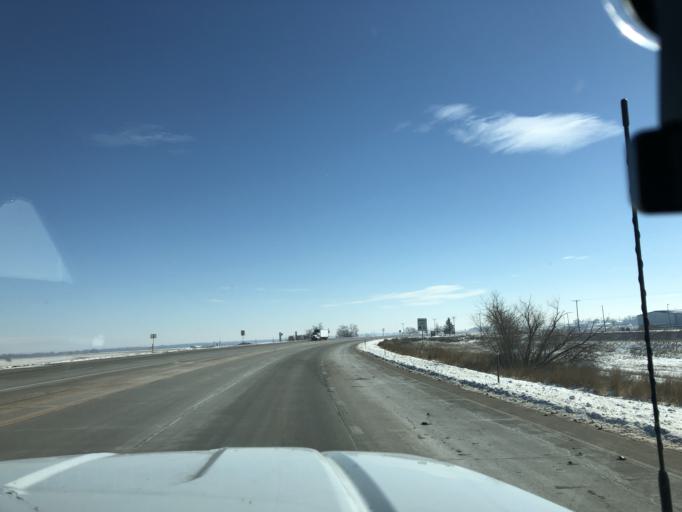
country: US
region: Colorado
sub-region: Weld County
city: Kersey
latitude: 40.3930
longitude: -104.5539
